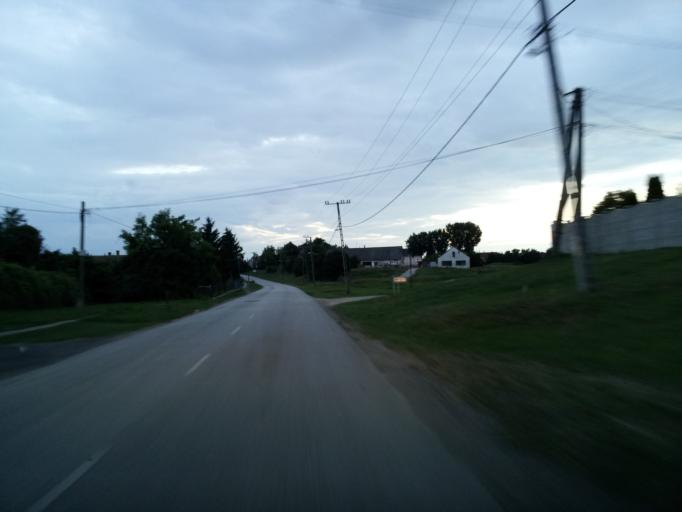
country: HU
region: Somogy
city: Adand
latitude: 46.8391
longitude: 18.1052
